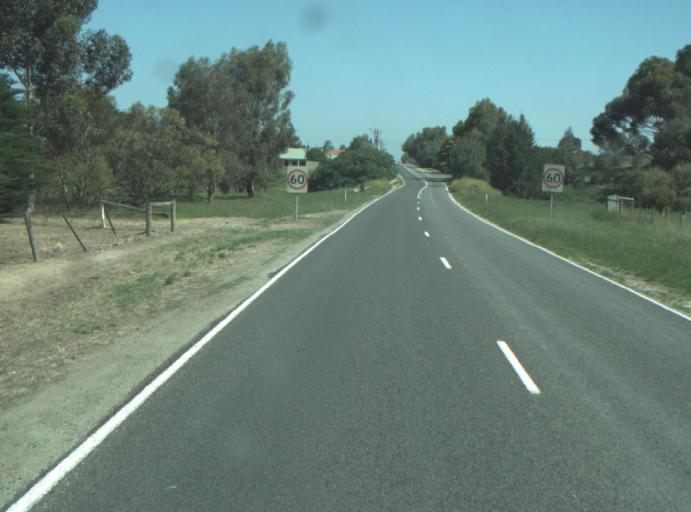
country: AU
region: Victoria
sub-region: Greater Geelong
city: Lara
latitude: -38.0156
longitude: 144.3977
